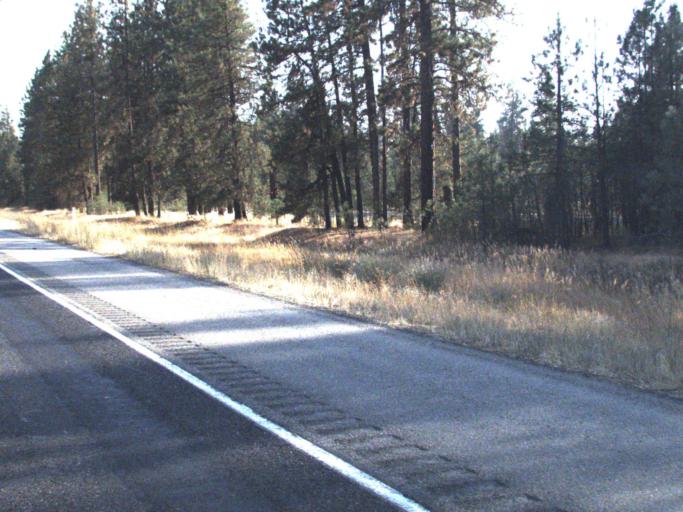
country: US
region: Washington
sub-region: Spokane County
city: Mead
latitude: 47.8481
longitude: -117.3550
